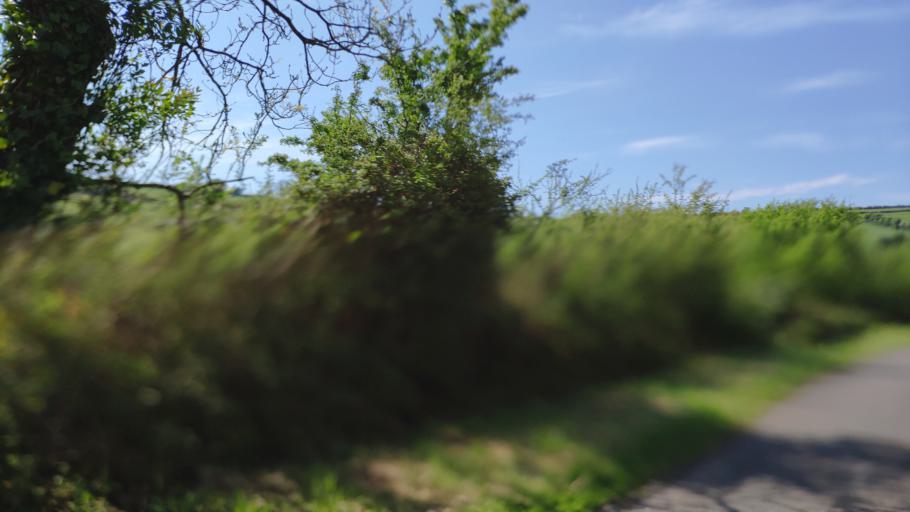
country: IE
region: Munster
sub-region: County Cork
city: Blarney
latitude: 51.9139
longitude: -8.5200
